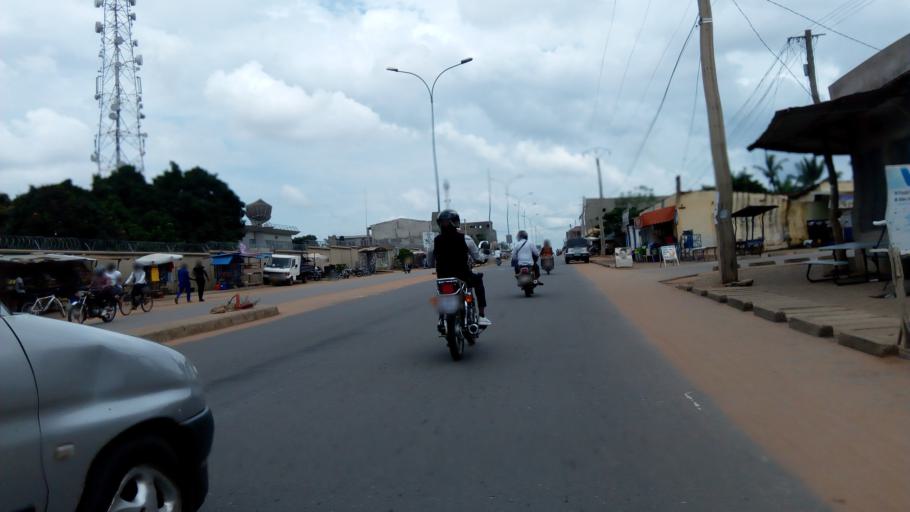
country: TG
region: Maritime
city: Lome
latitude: 6.2121
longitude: 1.1764
